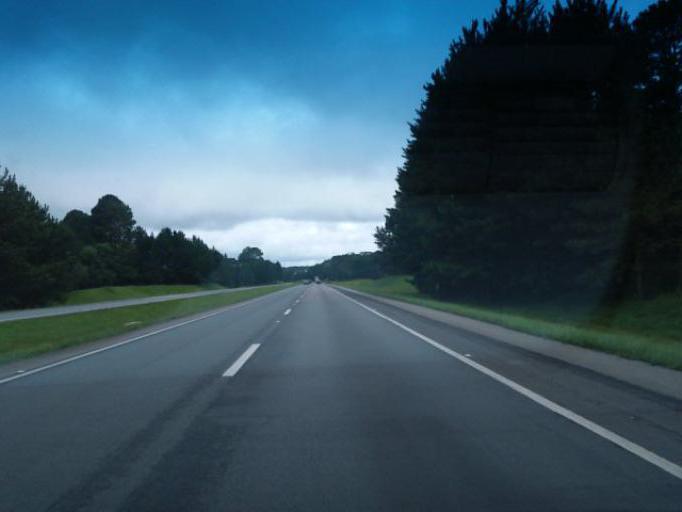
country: BR
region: Parana
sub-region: Piraquara
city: Piraquara
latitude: -25.4134
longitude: -49.0661
